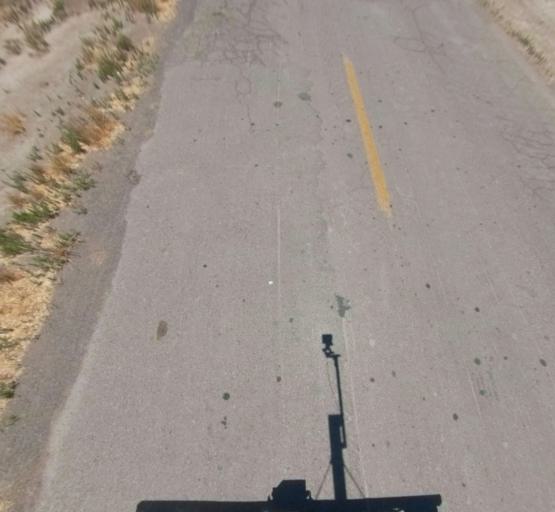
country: US
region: California
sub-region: Merced County
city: Dos Palos
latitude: 37.0546
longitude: -120.4804
